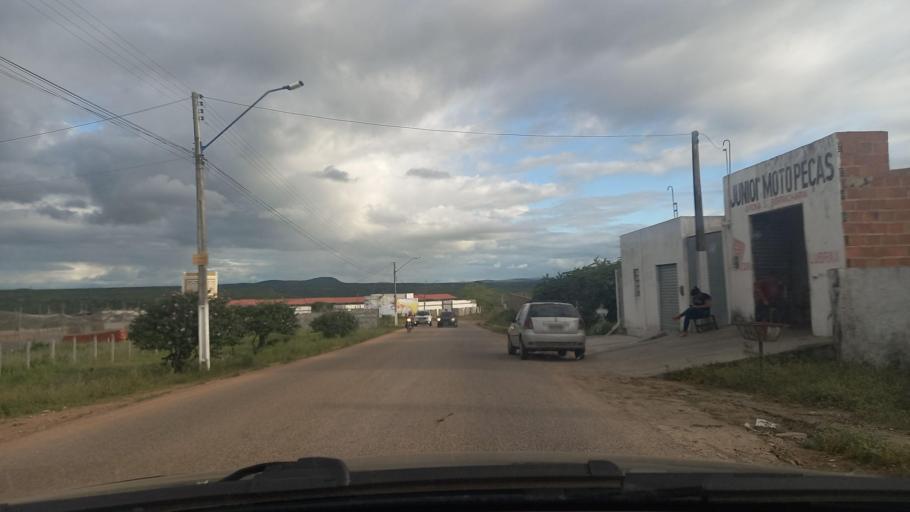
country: BR
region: Sergipe
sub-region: Caninde De Sao Francisco
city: Caninde de Sao Francisco
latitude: -9.6142
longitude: -37.7621
